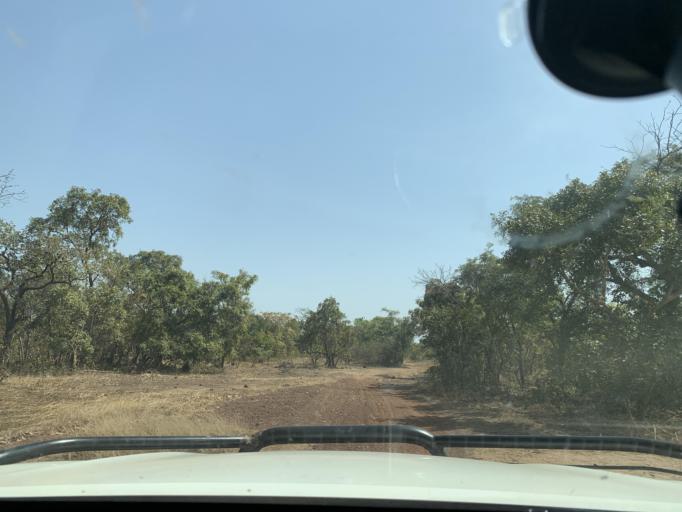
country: ML
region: Sikasso
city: Kolondieba
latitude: 10.8361
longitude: -6.7937
